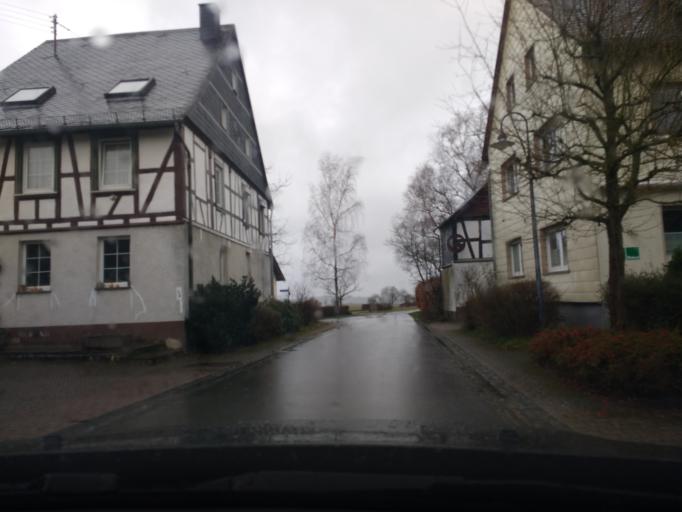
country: DE
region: Rheinland-Pfalz
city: Kleinich
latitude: 49.9154
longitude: 7.1830
